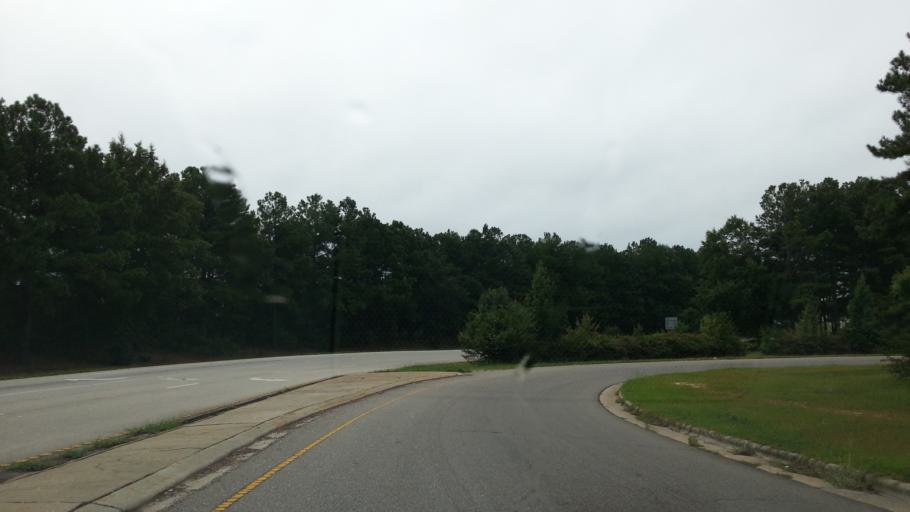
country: US
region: North Carolina
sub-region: Cumberland County
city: Fort Bragg
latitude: 35.0775
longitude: -78.9584
